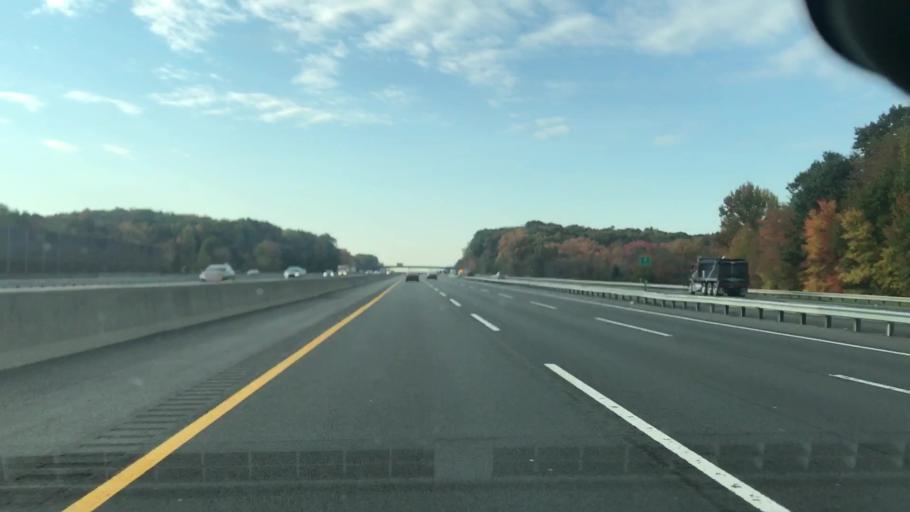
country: US
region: New Jersey
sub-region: Middlesex County
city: East Brunswick
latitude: 40.4079
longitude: -74.4503
